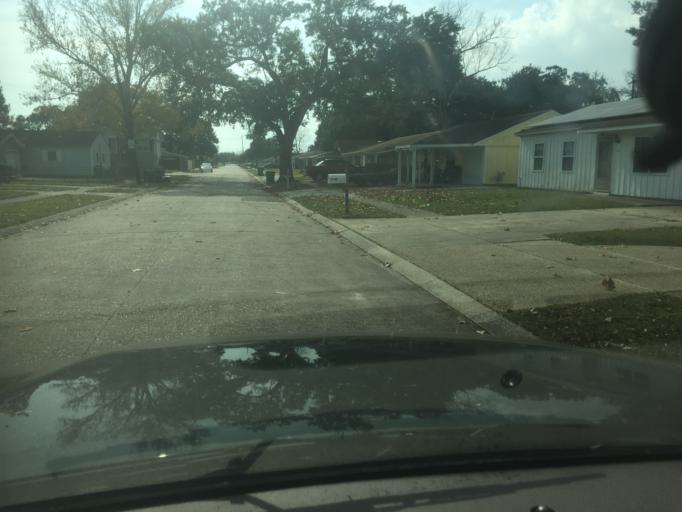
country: US
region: Louisiana
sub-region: Jefferson Parish
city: Avondale
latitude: 29.9141
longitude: -90.2056
